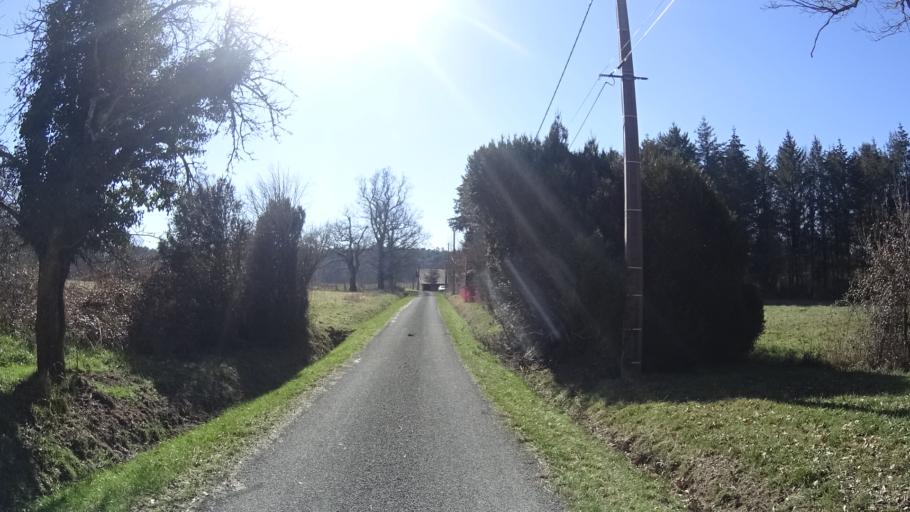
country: FR
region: Aquitaine
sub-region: Departement de la Dordogne
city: Saint-Aulaye
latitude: 45.1428
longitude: 0.2084
